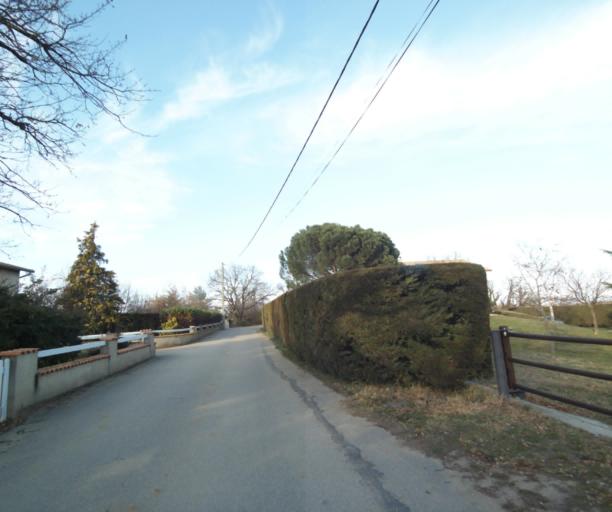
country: FR
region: Rhone-Alpes
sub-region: Departement de l'Ardeche
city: Davezieux
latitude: 45.2590
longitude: 4.7151
